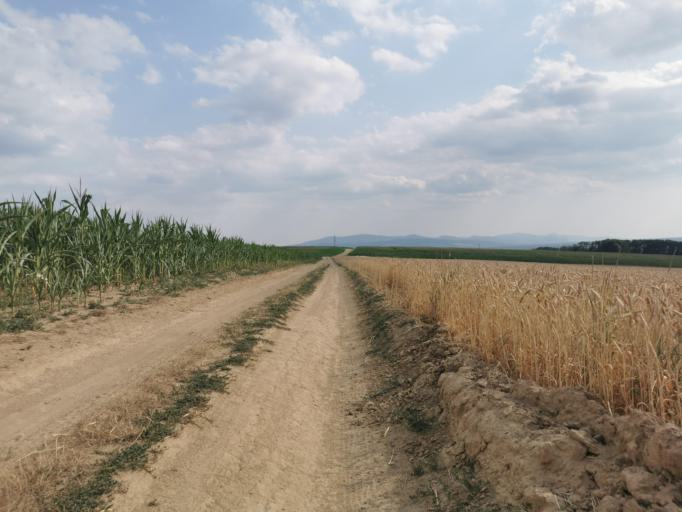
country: SK
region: Trnavsky
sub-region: Okres Senica
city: Senica
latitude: 48.6945
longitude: 17.4212
